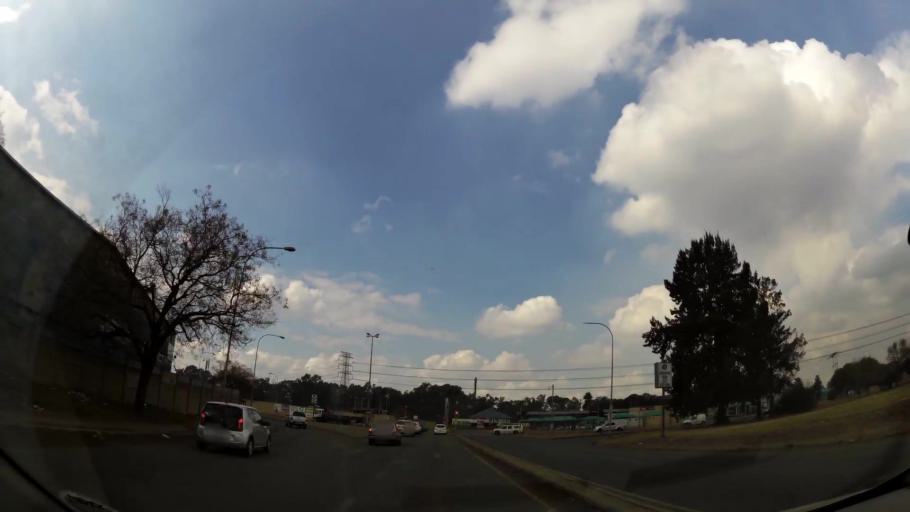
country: ZA
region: Gauteng
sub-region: Sedibeng District Municipality
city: Vereeniging
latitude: -26.6694
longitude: 27.9389
